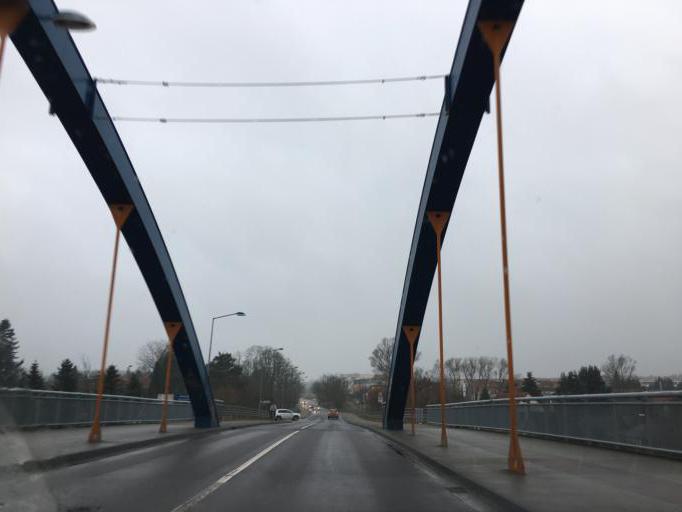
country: DE
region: Saxony-Anhalt
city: Haldensleben I
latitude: 52.2827
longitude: 11.3994
